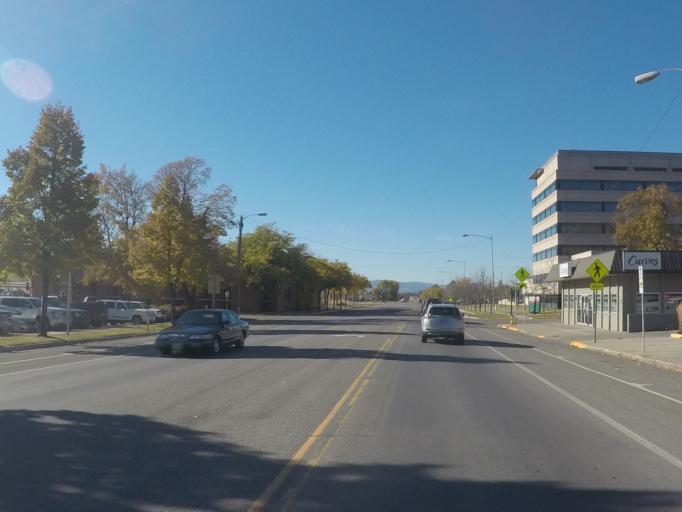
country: US
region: Montana
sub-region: Missoula County
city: Missoula
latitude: 46.8737
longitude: -113.9992
